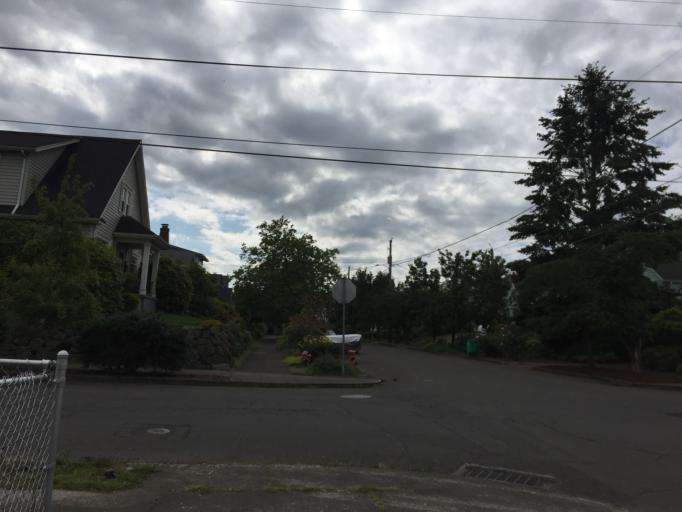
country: US
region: Oregon
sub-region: Multnomah County
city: Portland
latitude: 45.5312
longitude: -122.6100
